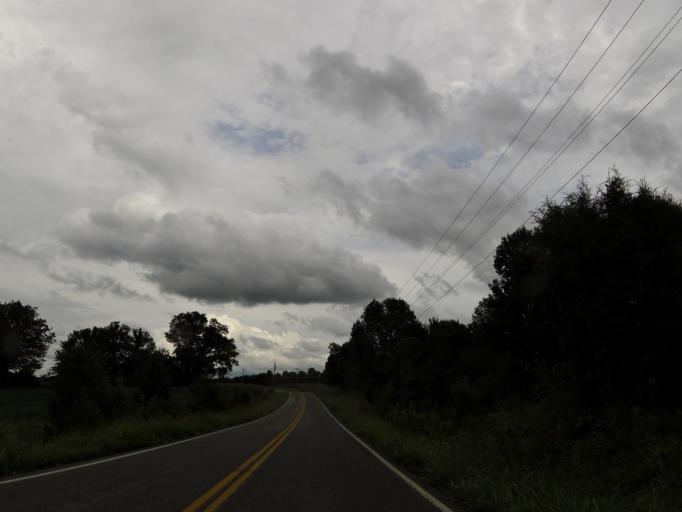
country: US
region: Kentucky
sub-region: Ballard County
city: Wickliffe
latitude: 36.9791
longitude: -89.0134
